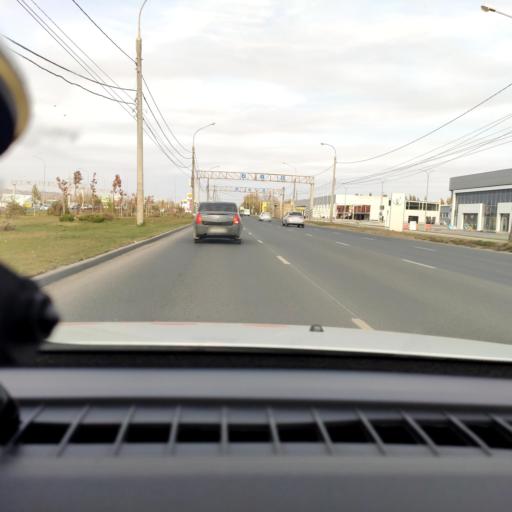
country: RU
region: Samara
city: Samara
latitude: 53.1397
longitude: 50.1785
